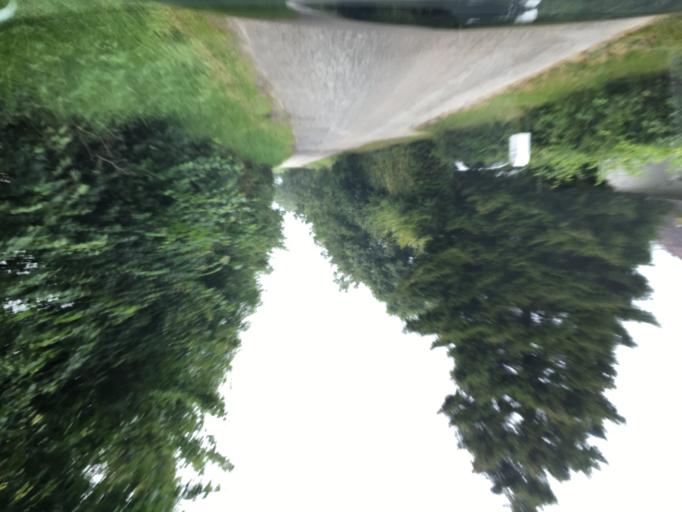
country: DK
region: South Denmark
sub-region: Kolding Kommune
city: Kolding
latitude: 55.5651
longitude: 9.4410
